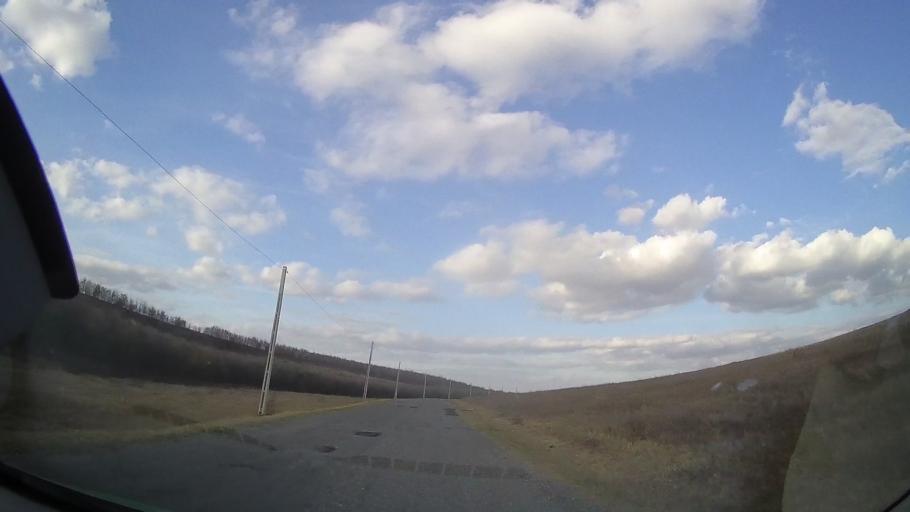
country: RO
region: Constanta
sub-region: Comuna Cerchezu
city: Cerchezu
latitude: 43.8304
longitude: 28.0963
